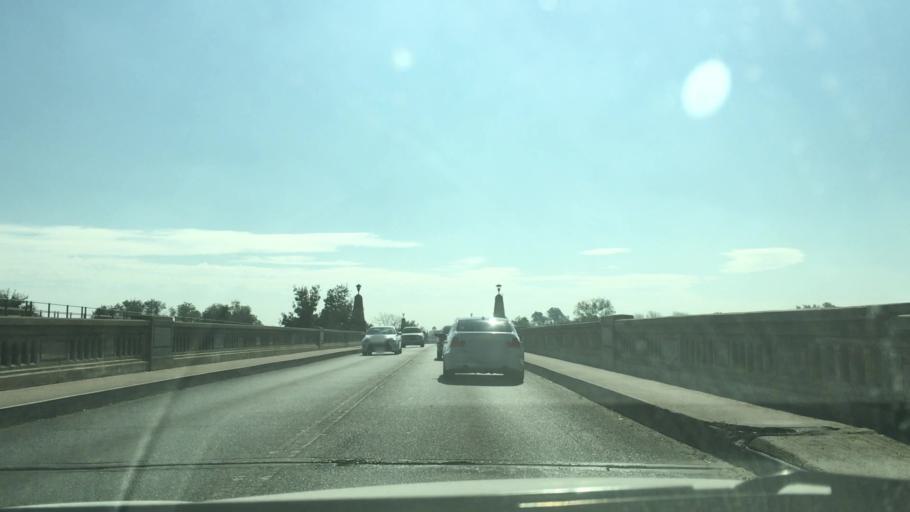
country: US
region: California
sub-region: Stanislaus County
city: Modesto
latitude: 37.6289
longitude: -120.9943
